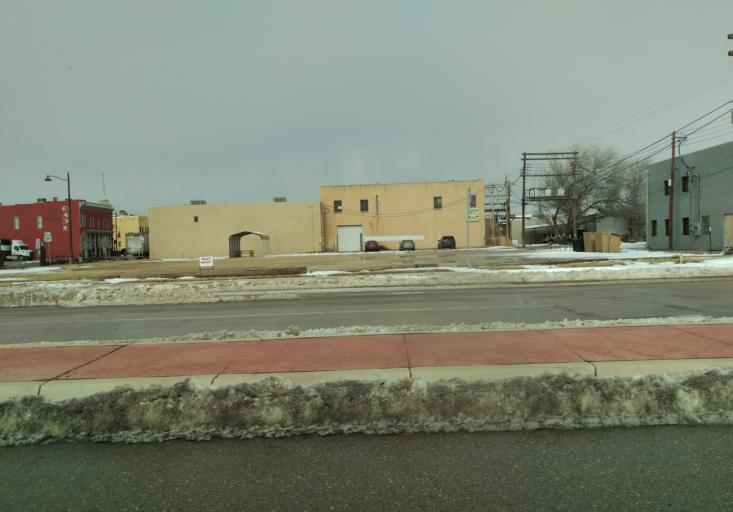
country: US
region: New Mexico
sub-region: Eddy County
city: Carlsbad
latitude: 32.4179
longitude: -104.2286
